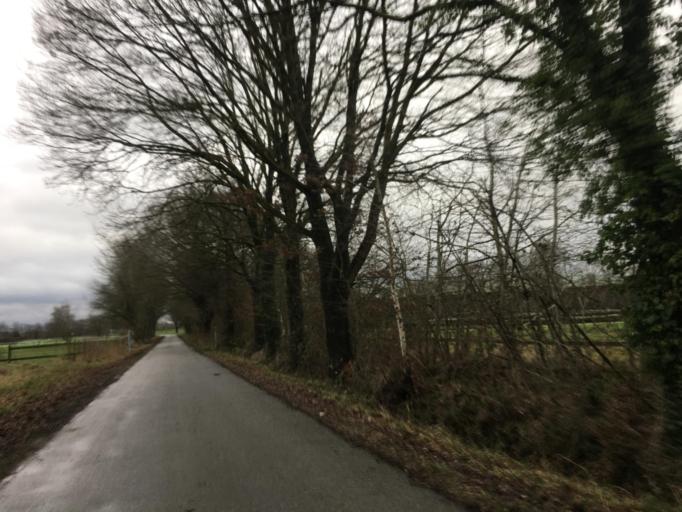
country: DE
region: North Rhine-Westphalia
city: Olfen
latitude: 51.7706
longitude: 7.3767
